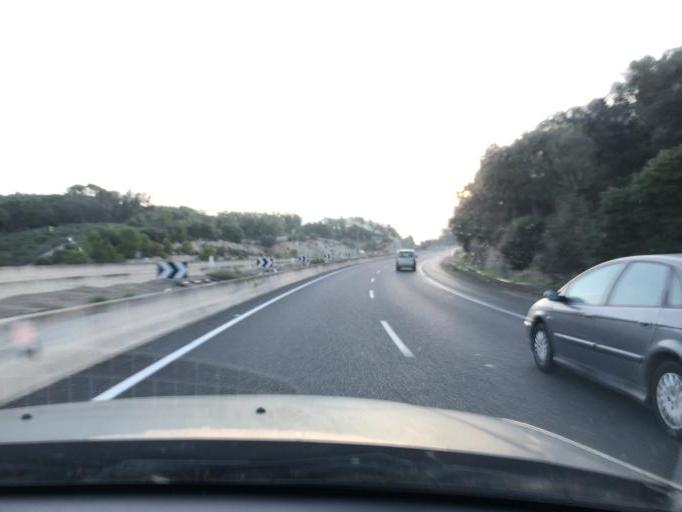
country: ES
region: Balearic Islands
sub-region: Illes Balears
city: Montuiri
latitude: 39.5607
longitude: 3.0022
